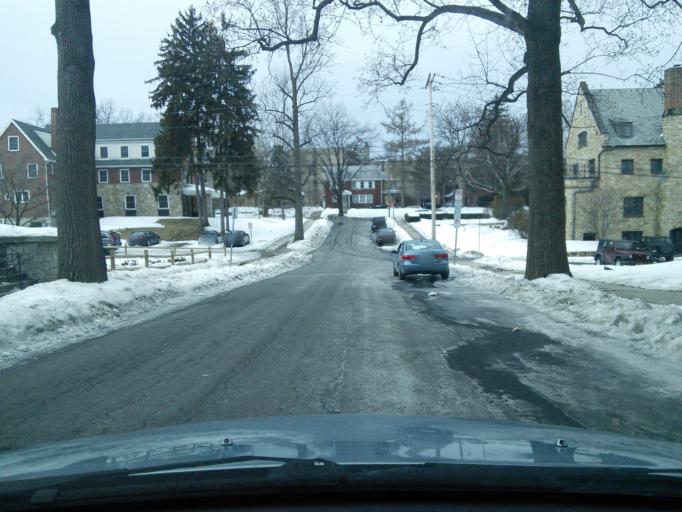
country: US
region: Pennsylvania
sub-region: Centre County
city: State College
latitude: 40.7951
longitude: -77.8540
